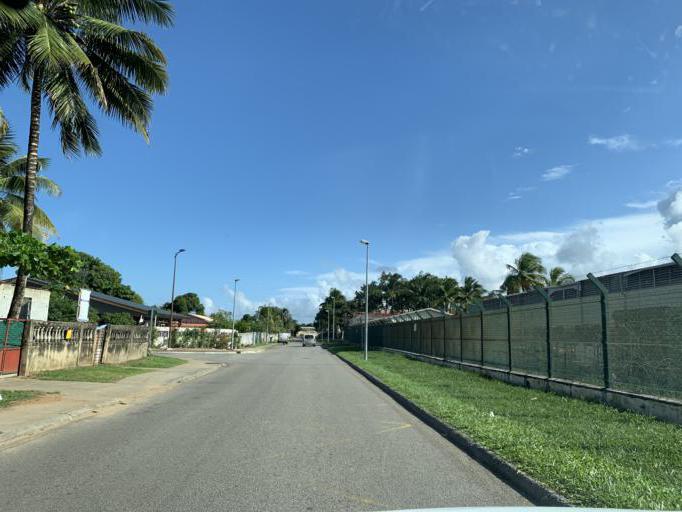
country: GF
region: Guyane
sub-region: Guyane
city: Kourou
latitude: 5.1721
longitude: -52.6463
